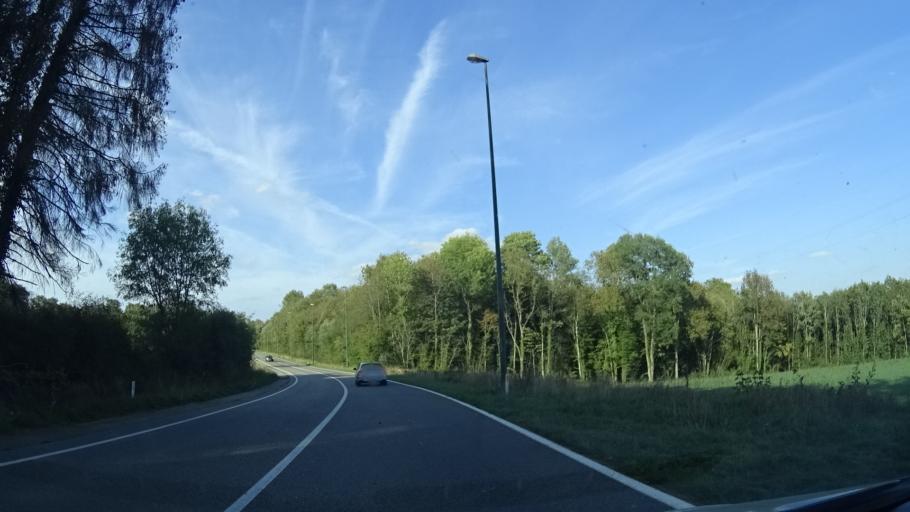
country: BE
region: Wallonia
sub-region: Province de Namur
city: Cerfontaine
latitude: 50.2078
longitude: 4.3809
